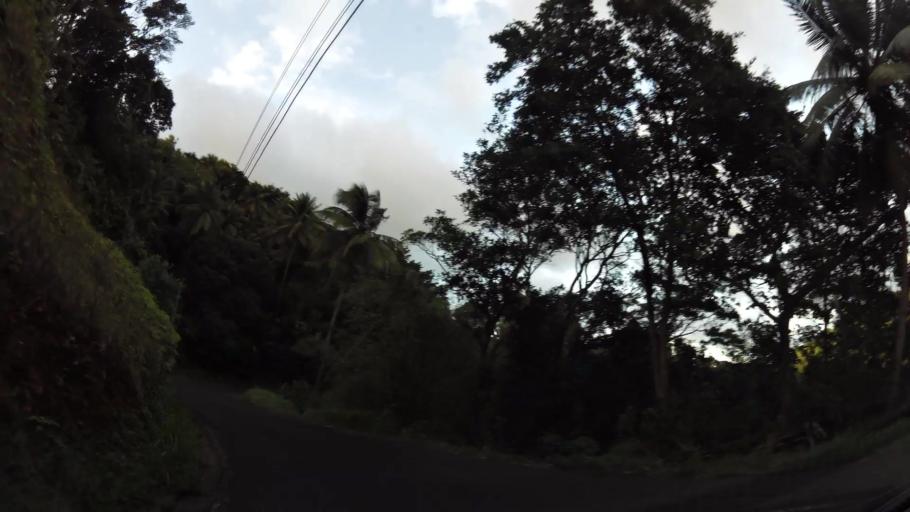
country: DM
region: Saint John
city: Portsmouth
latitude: 15.5817
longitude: -61.4163
